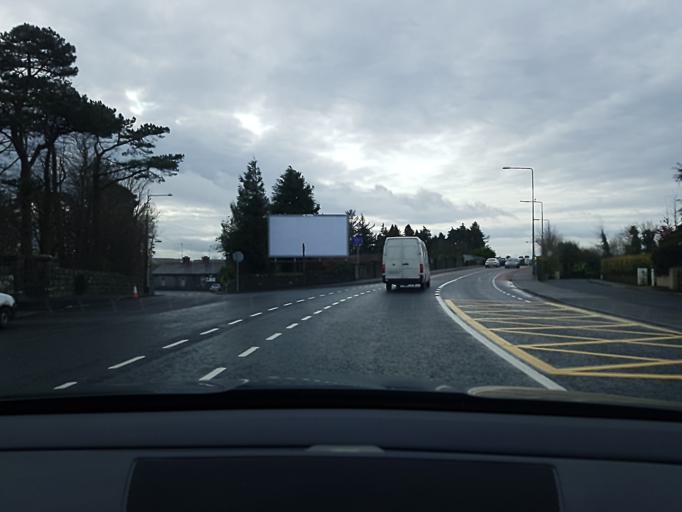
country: IE
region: Connaught
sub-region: Maigh Eo
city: Castlebar
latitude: 53.8484
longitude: -9.2886
